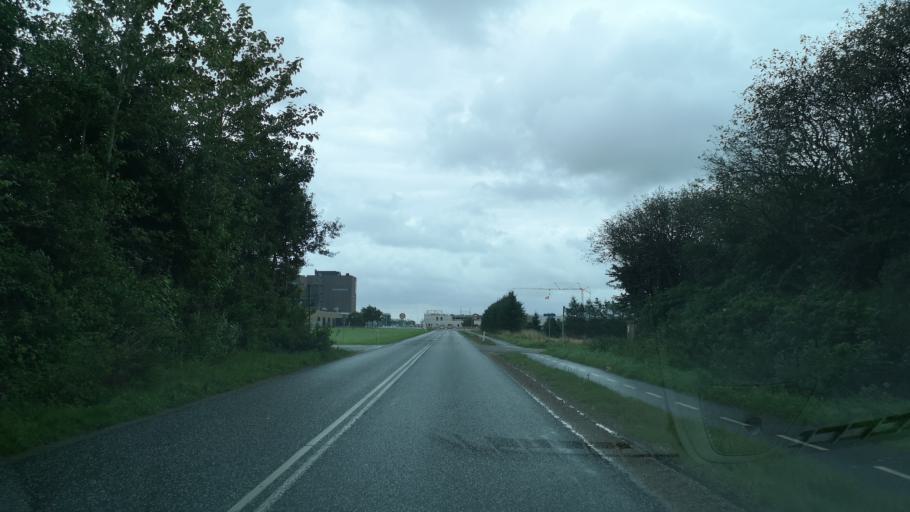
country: DK
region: Central Jutland
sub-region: Ringkobing-Skjern Kommune
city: Videbaek
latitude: 56.0485
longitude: 8.6603
